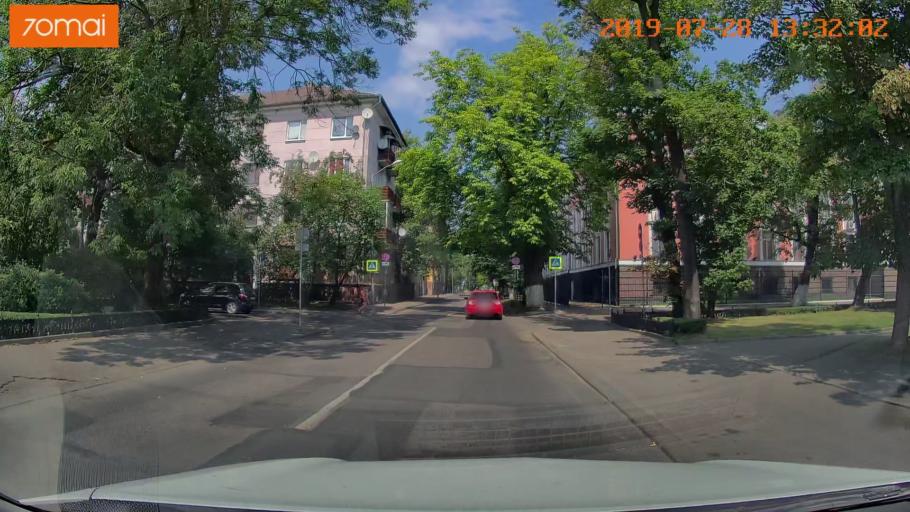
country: RU
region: Kaliningrad
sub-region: Gorod Kaliningrad
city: Kaliningrad
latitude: 54.7204
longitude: 20.4942
